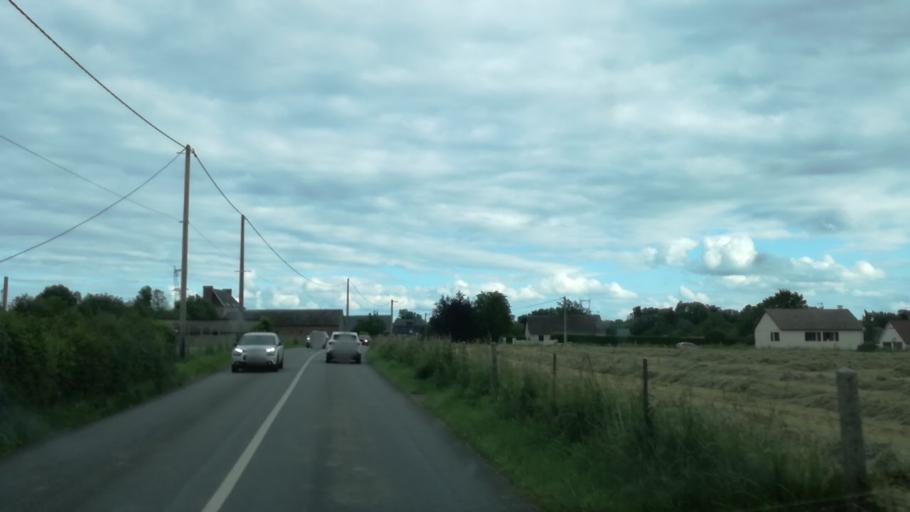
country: FR
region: Haute-Normandie
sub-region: Departement de l'Eure
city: Le Neubourg
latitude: 49.2151
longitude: 0.8477
